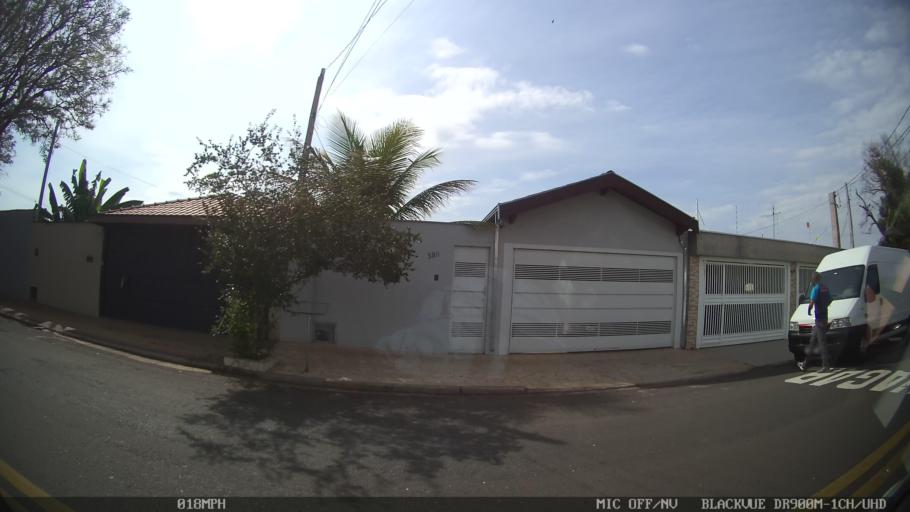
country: BR
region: Sao Paulo
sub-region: Piracicaba
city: Piracicaba
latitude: -22.7146
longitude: -47.6675
